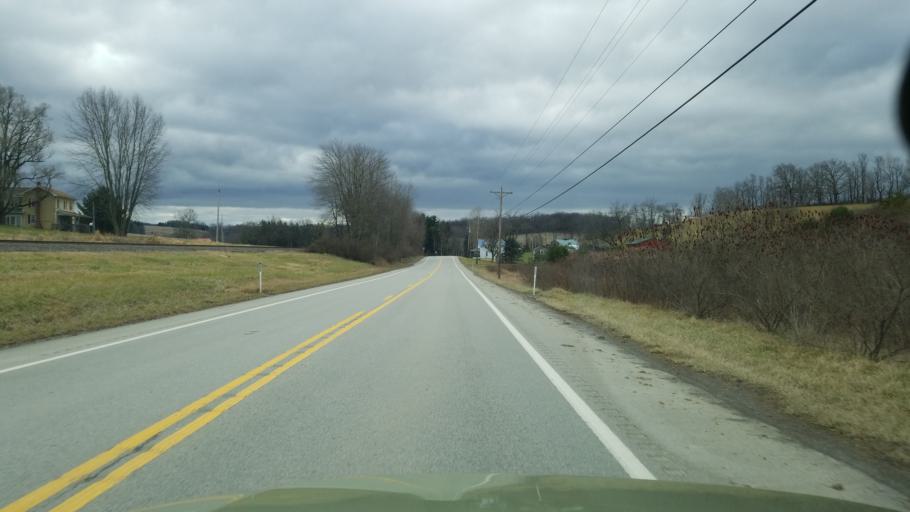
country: US
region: Pennsylvania
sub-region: Indiana County
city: Clymer
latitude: 40.7923
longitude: -79.0541
